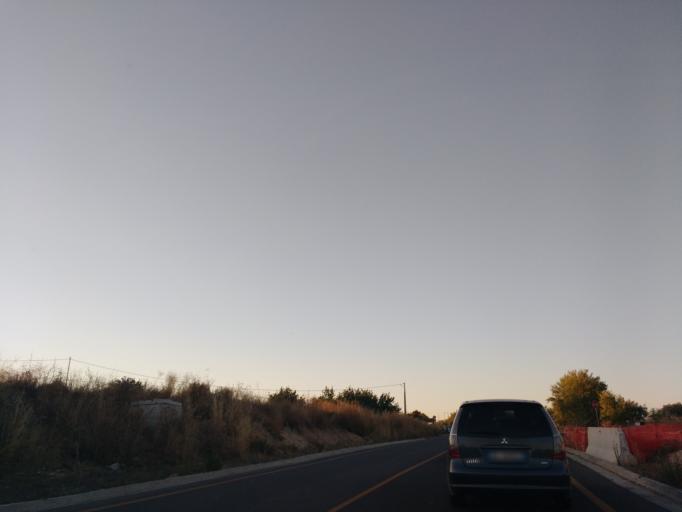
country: IT
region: Sicily
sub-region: Ragusa
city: Ispica
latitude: 36.7735
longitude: 14.9244
